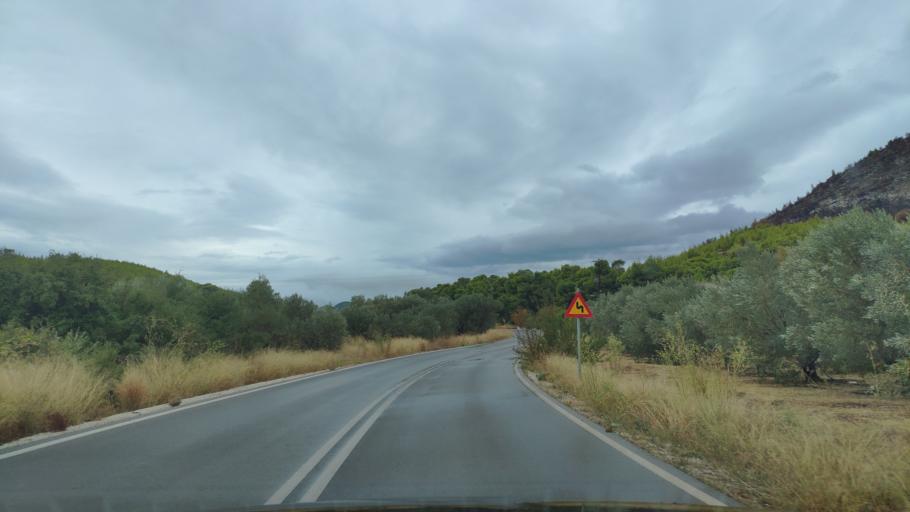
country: GR
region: Peloponnese
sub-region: Nomos Korinthias
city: Perachora
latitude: 38.0287
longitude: 22.9339
